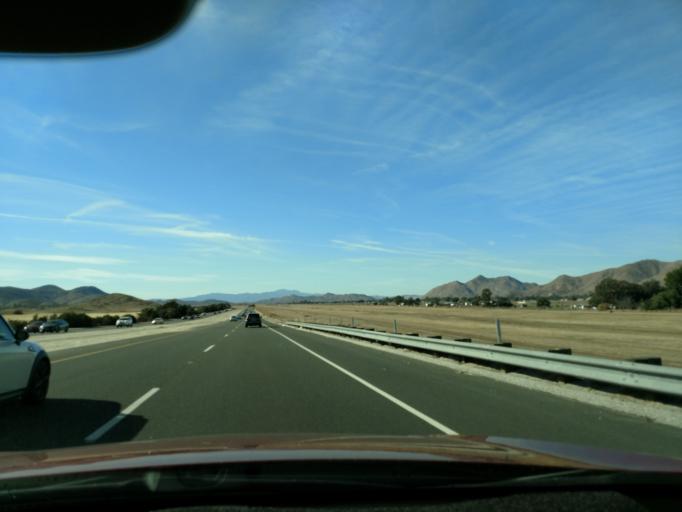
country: US
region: California
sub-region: Riverside County
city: Winchester
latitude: 33.6986
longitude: -117.0504
